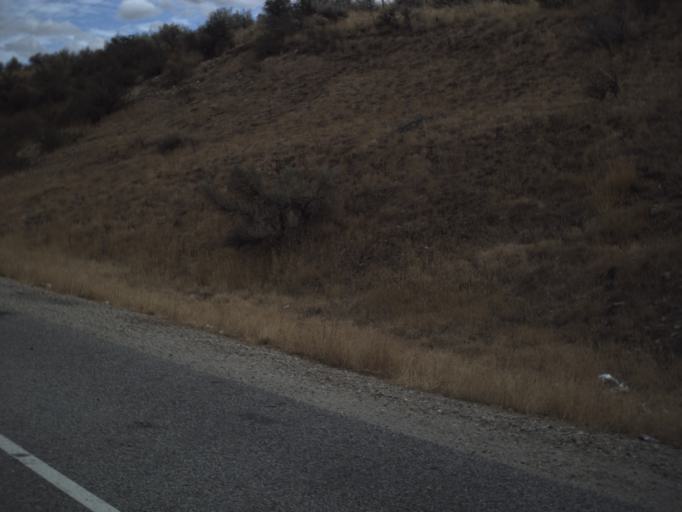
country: US
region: Utah
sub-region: Box Elder County
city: Garland
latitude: 41.8967
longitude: -112.5437
